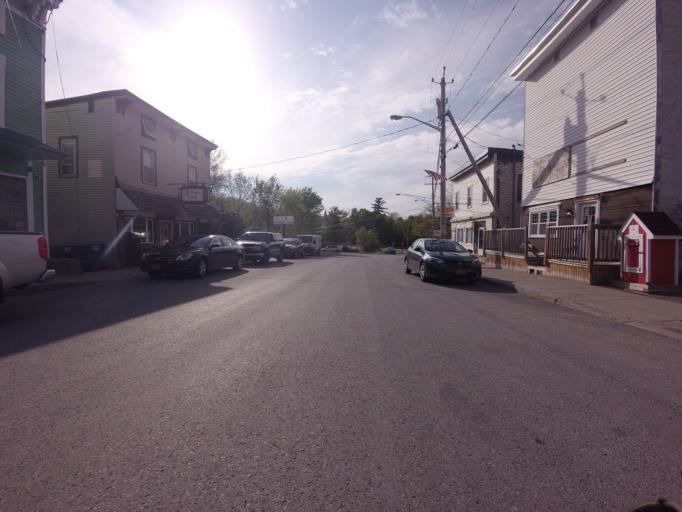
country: US
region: New York
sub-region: St. Lawrence County
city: Gouverneur
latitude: 44.1485
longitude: -75.3162
